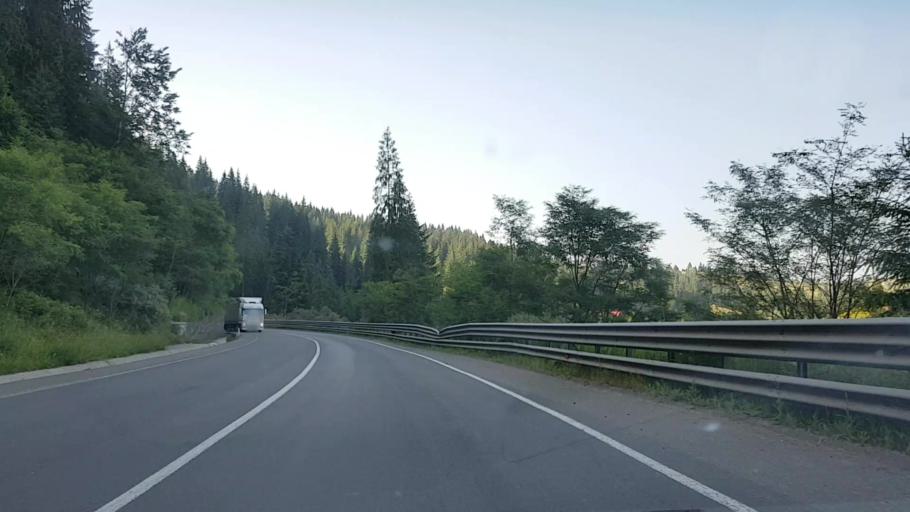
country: RO
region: Bistrita-Nasaud
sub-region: Comuna Lunca Ilvei
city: Lunca Ilvei
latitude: 47.2287
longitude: 24.9635
